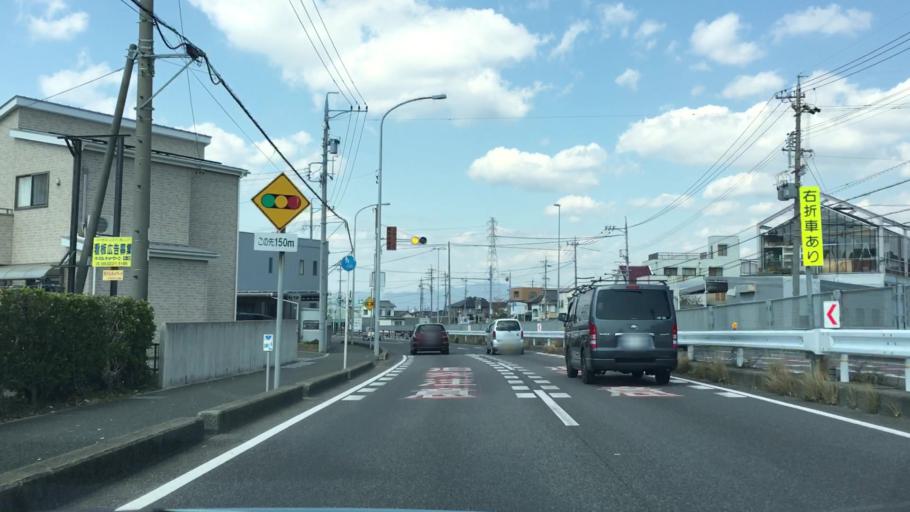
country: JP
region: Aichi
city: Toyohashi
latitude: 34.7364
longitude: 137.4243
